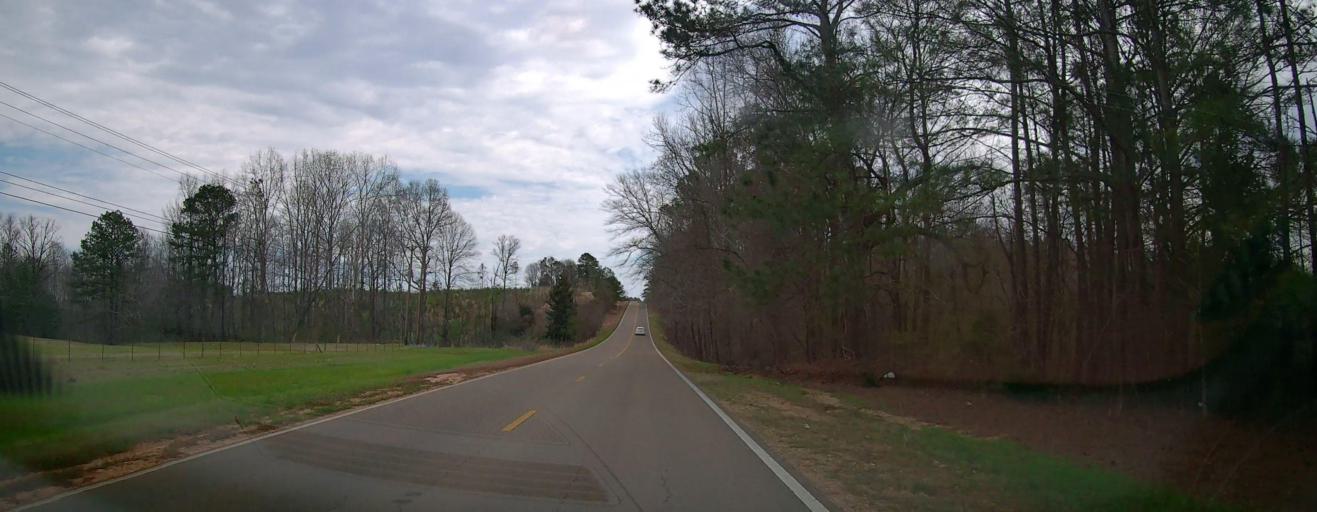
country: US
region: Mississippi
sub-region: Itawamba County
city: Fulton
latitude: 34.2774
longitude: -88.3638
